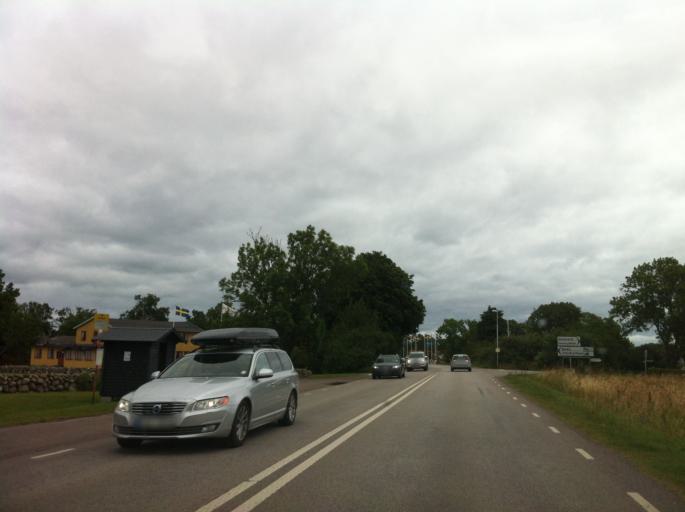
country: SE
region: Kalmar
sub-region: Borgholms Kommun
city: Borgholm
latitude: 57.2340
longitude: 17.0539
